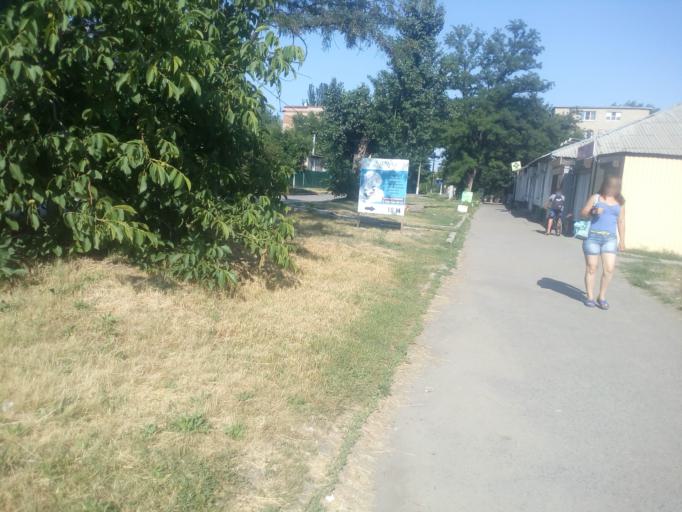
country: RU
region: Rostov
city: Sholokhovskiy
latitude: 48.2801
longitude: 41.0533
